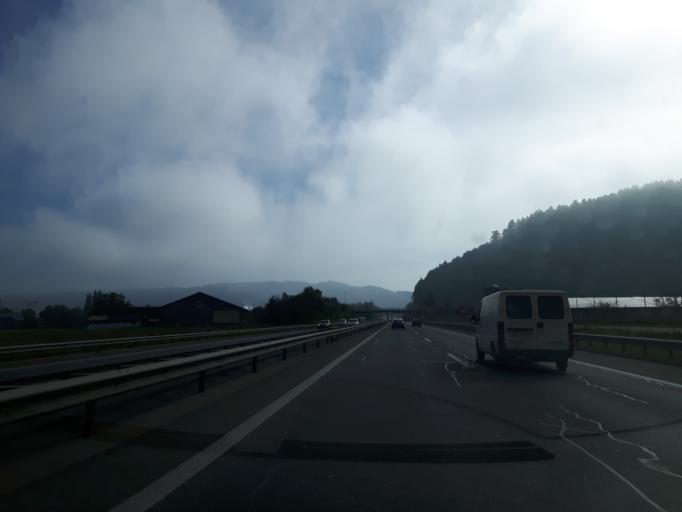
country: CH
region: Lucerne
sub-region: Willisau District
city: Dagmersellen
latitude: 47.2234
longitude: 7.9735
